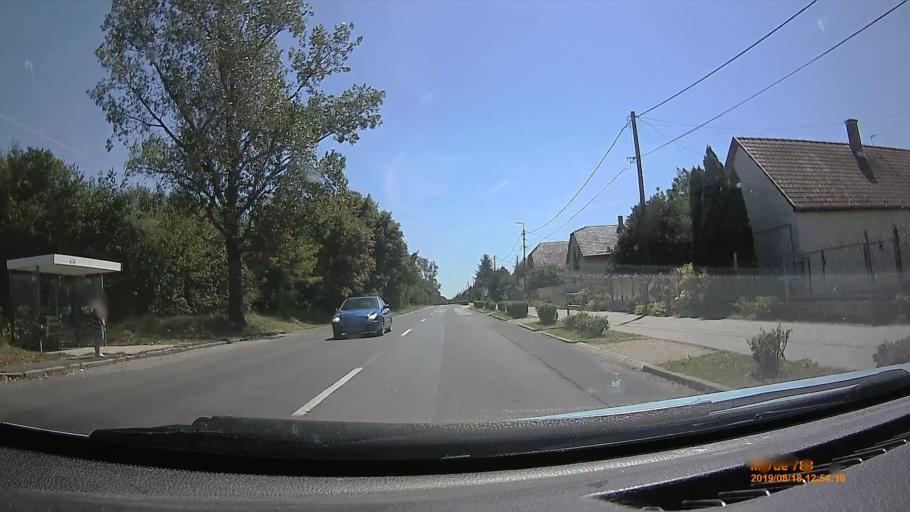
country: HU
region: Fejer
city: Aba
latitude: 47.0429
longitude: 18.5304
